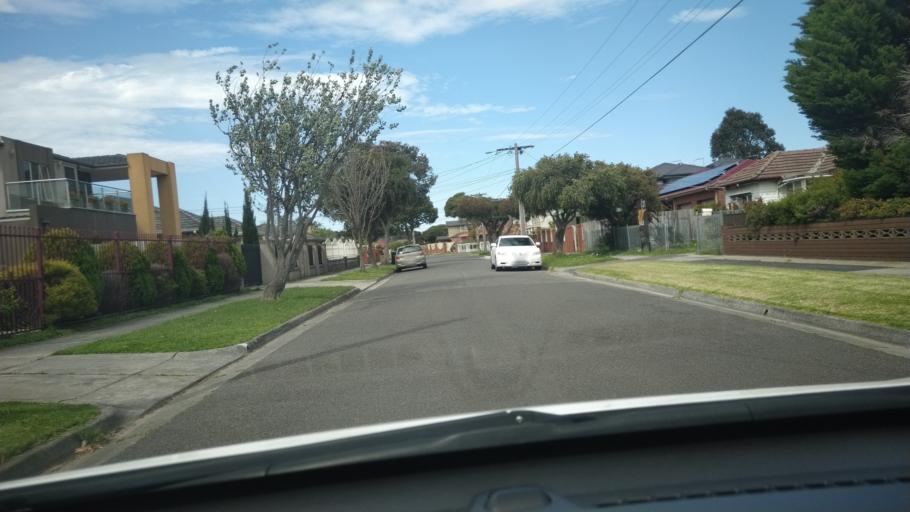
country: AU
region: Victoria
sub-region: Greater Dandenong
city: Springvale
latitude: -37.9546
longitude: 145.1558
